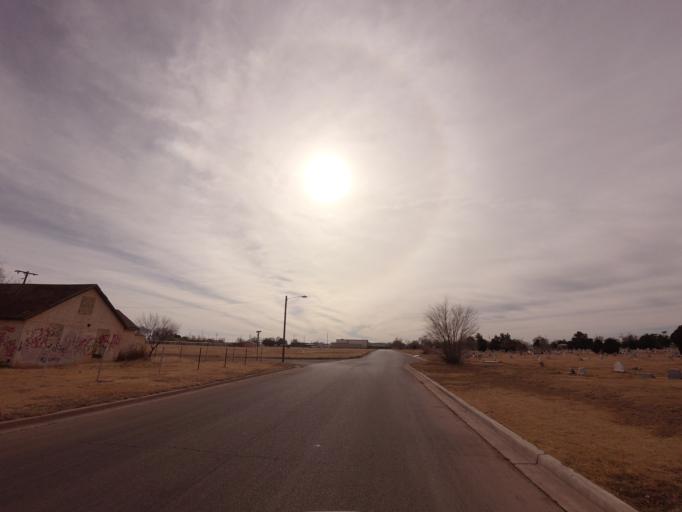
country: US
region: New Mexico
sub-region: Curry County
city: Clovis
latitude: 34.4070
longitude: -103.2405
